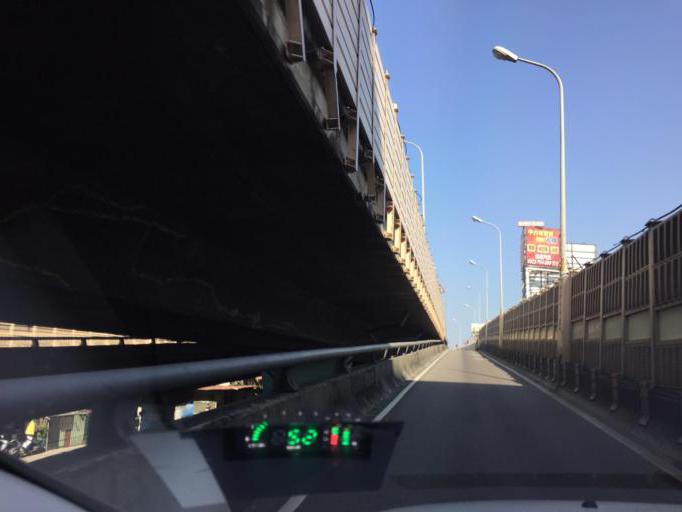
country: TW
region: Taipei
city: Taipei
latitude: 25.0614
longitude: 121.4847
